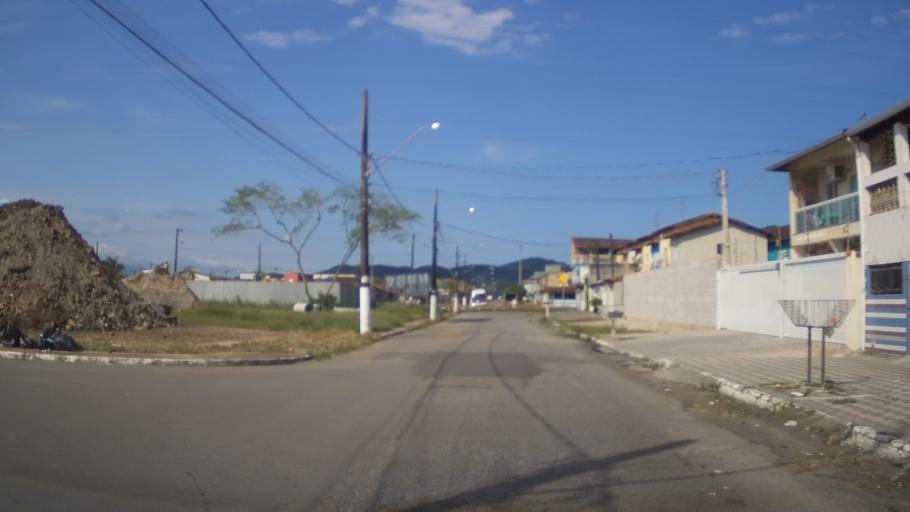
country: BR
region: Sao Paulo
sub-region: Praia Grande
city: Praia Grande
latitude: -23.9981
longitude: -46.4281
